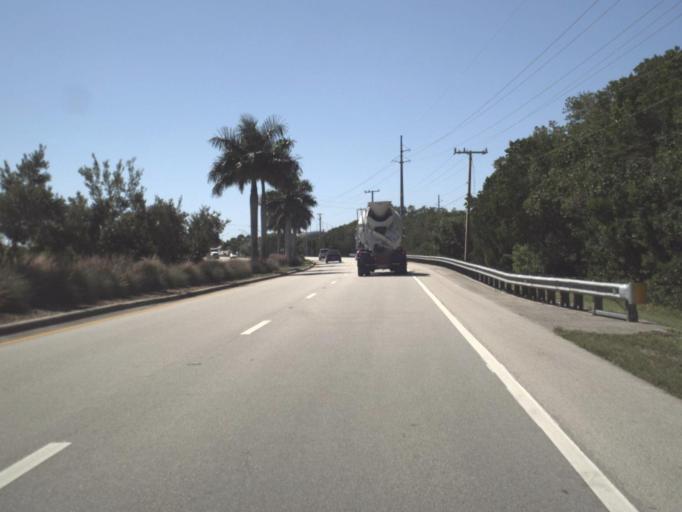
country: US
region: Florida
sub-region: Collier County
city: Marco
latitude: 25.9713
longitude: -81.7074
